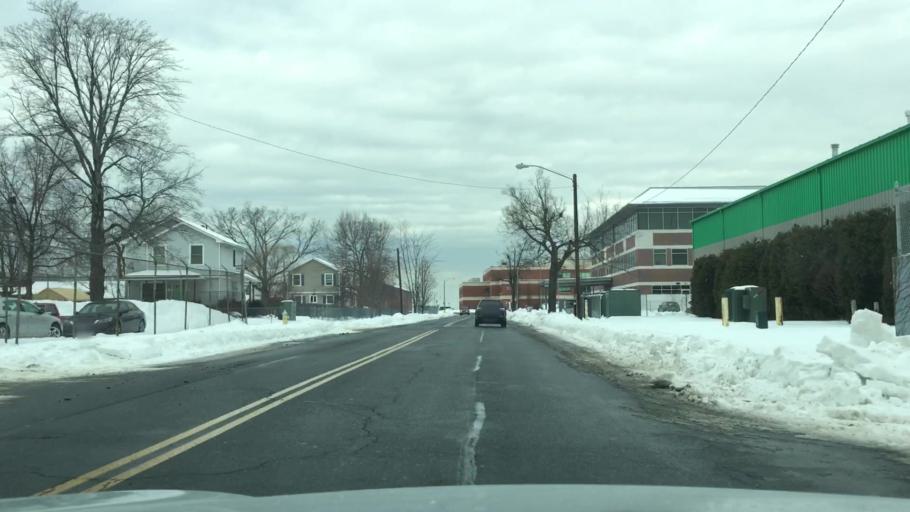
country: US
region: Massachusetts
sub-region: Hampden County
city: West Springfield
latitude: 42.1226
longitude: -72.6134
